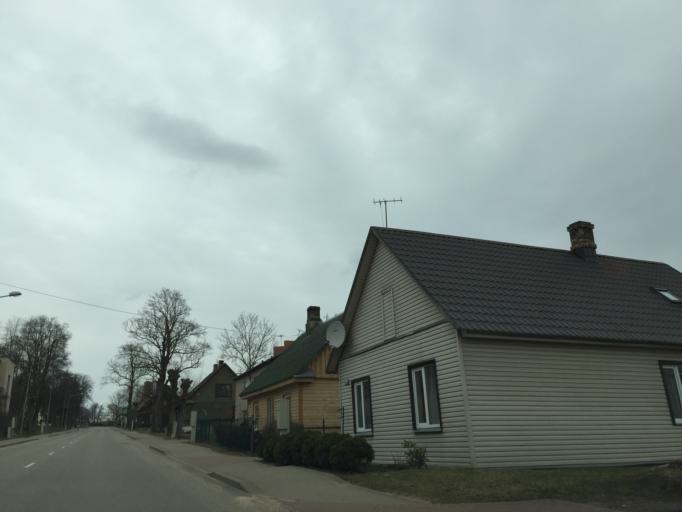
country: LV
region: Ilukste
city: Ilukste
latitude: 55.9809
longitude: 26.2922
